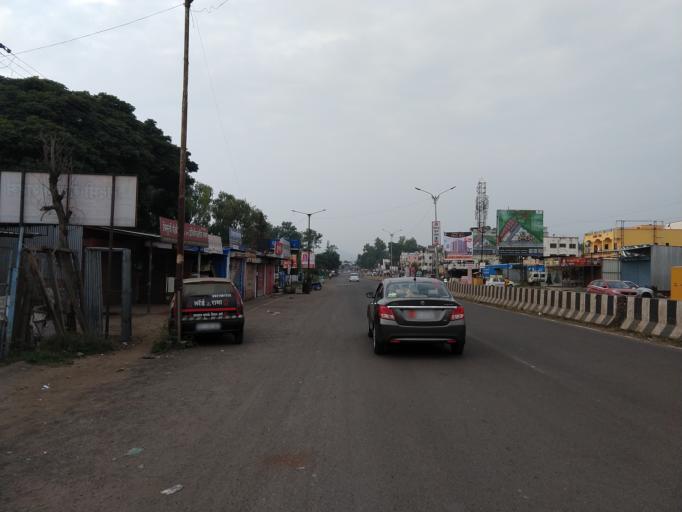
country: IN
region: Maharashtra
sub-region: Pune Division
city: Sasvad
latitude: 18.3526
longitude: 74.0287
